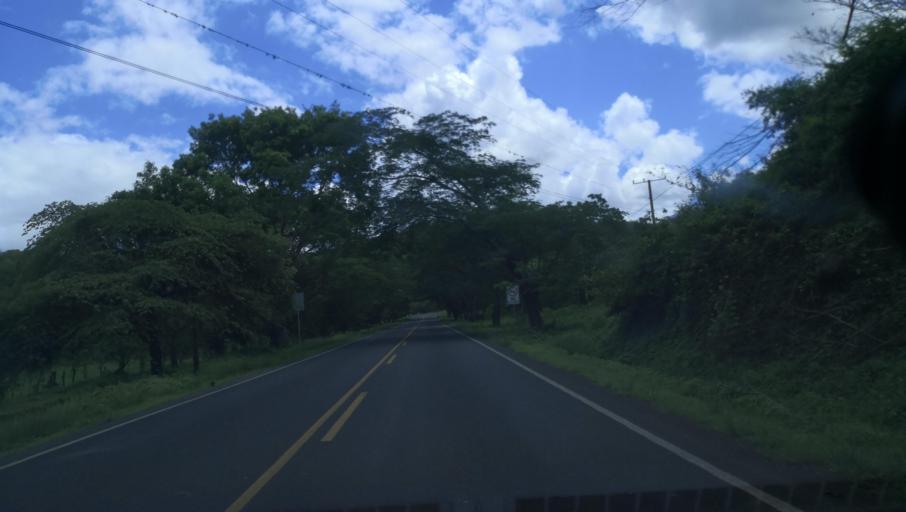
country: NI
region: Madriz
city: Palacaguina
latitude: 13.4340
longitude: -86.4222
